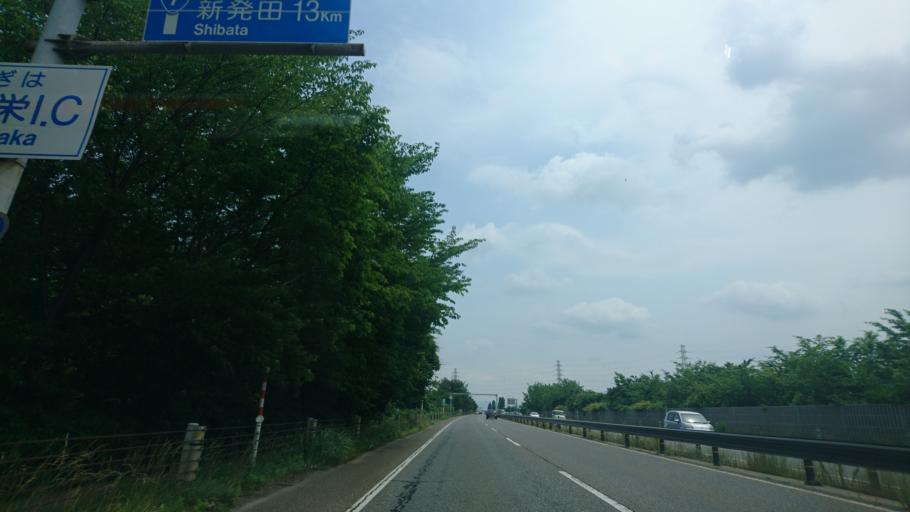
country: JP
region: Niigata
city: Kameda-honcho
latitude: 37.9447
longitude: 139.1884
